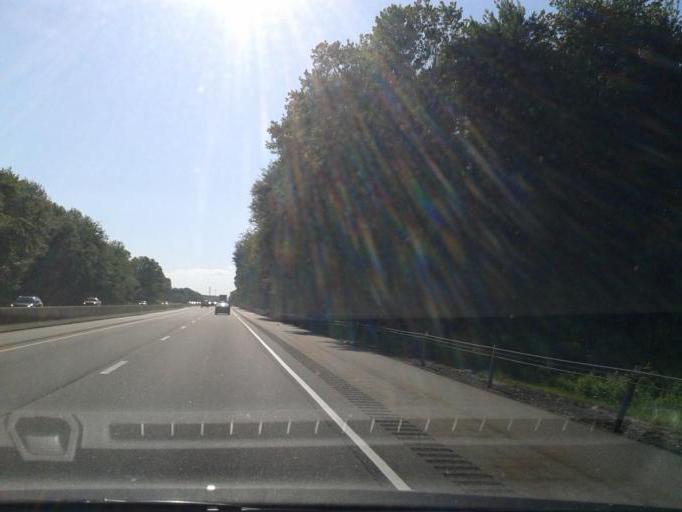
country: US
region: Connecticut
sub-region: New Haven County
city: Madison Center
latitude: 41.2884
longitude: -72.6288
